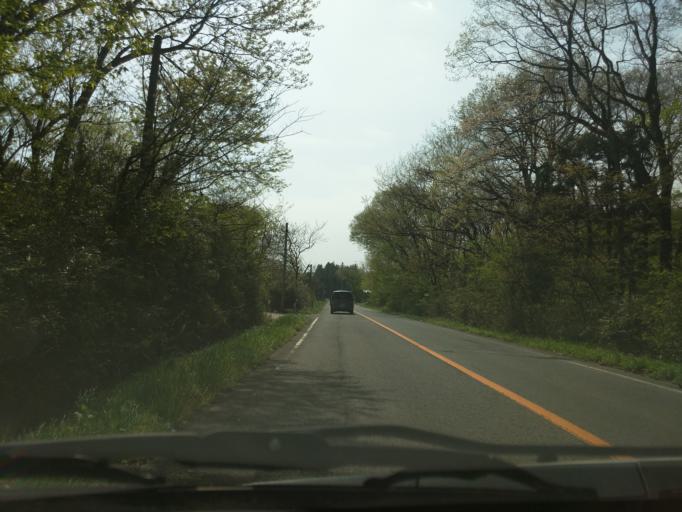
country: JP
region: Fukushima
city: Nihommatsu
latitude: 37.6006
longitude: 140.3765
